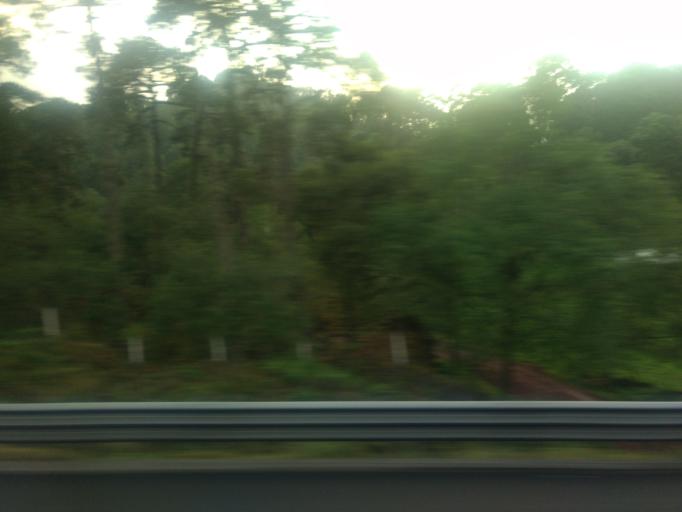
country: MX
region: Veracruz
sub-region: Acajete
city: La Joya
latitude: 19.6288
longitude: -97.0279
